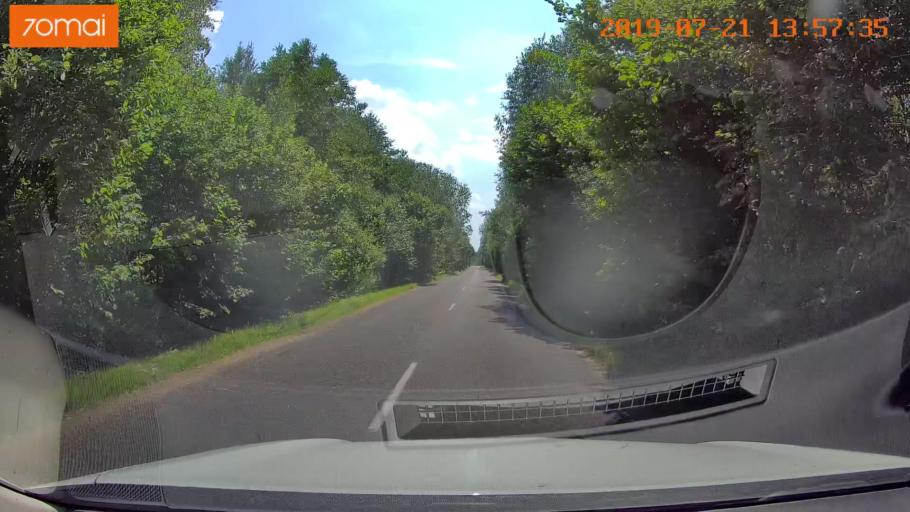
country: BY
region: Grodnenskaya
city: Lyubcha
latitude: 53.7709
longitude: 26.0876
